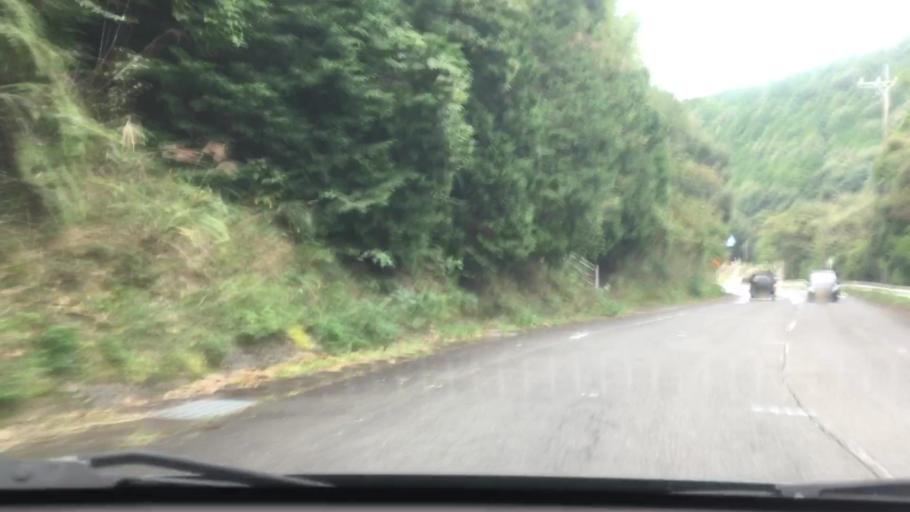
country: JP
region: Nagasaki
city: Sasebo
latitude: 32.9670
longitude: 129.6911
